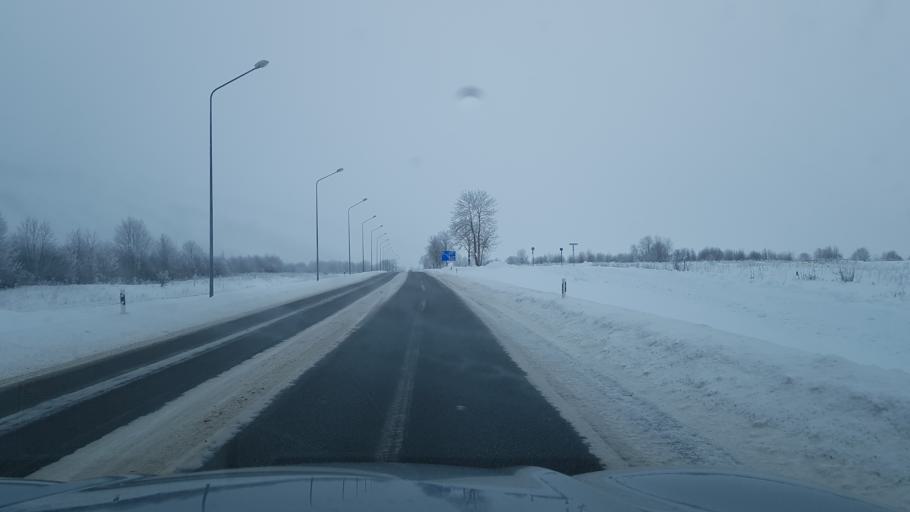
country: EE
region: Ida-Virumaa
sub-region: Johvi vald
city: Johvi
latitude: 59.3433
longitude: 27.4039
